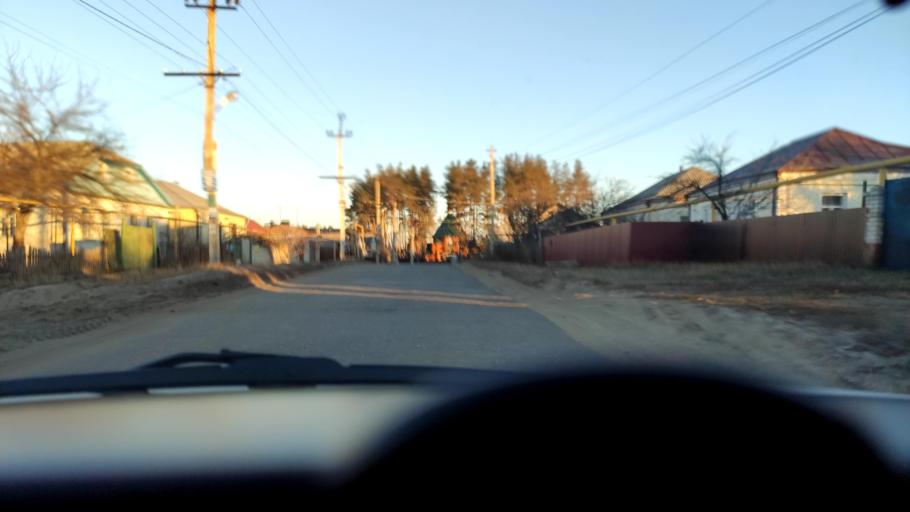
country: RU
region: Voronezj
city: Podgornoye
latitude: 51.7441
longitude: 39.1414
